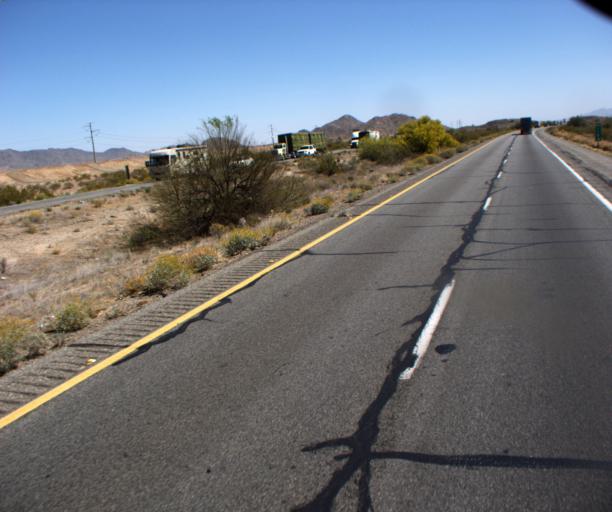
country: US
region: Arizona
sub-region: Maricopa County
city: Buckeye
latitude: 33.4350
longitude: -112.6593
